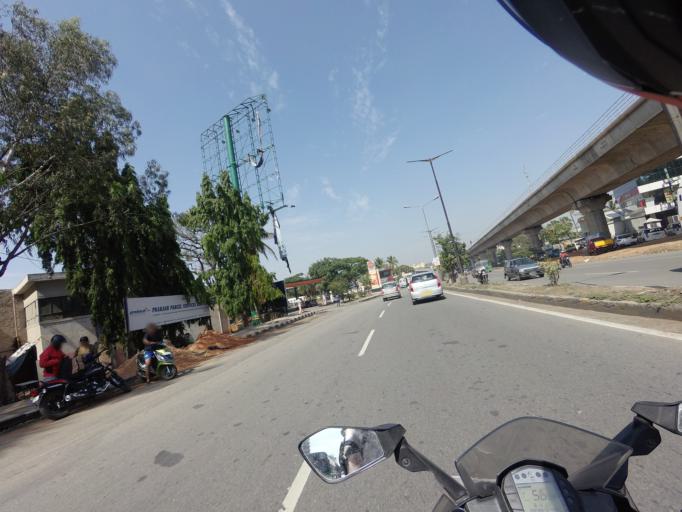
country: IN
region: Karnataka
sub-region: Bangalore Urban
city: Bangalore
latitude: 12.9477
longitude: 77.5341
